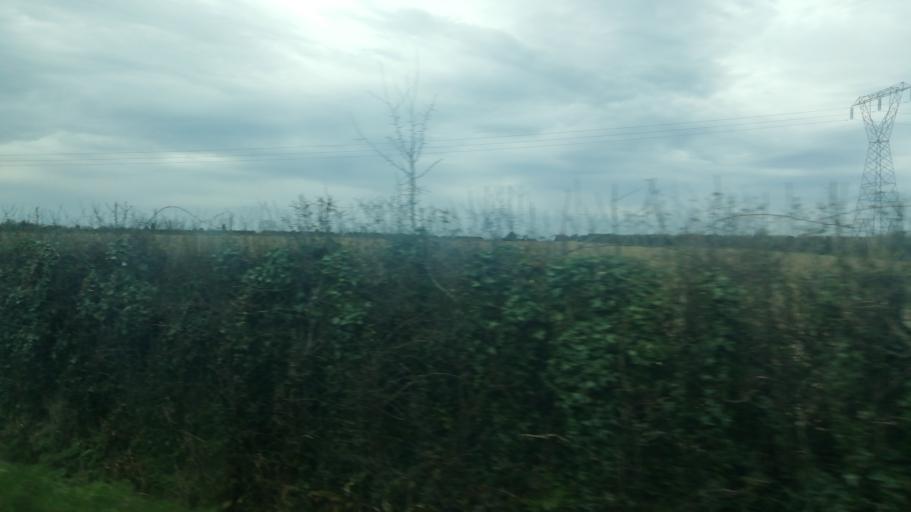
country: IE
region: Leinster
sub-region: Kildare
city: Prosperous
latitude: 53.3050
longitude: -6.7275
